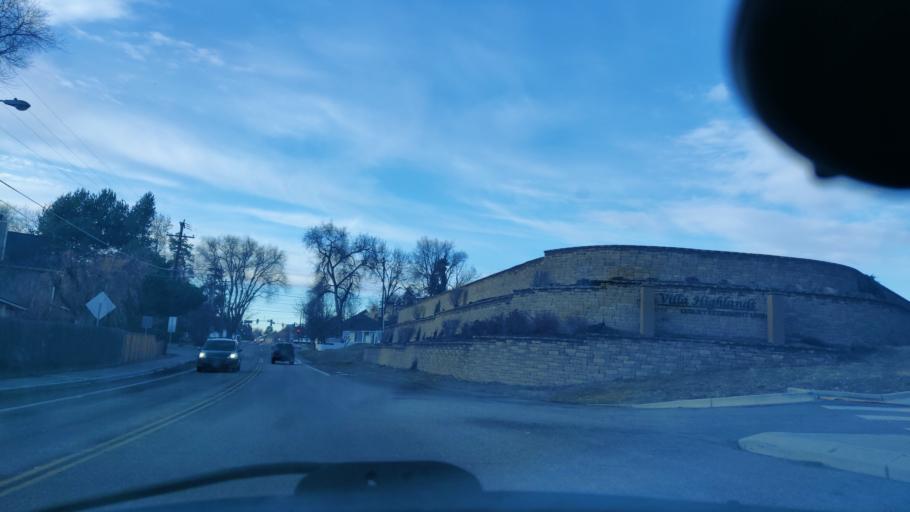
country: US
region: Idaho
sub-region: Ada County
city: Boise
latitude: 43.6391
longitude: -116.2061
